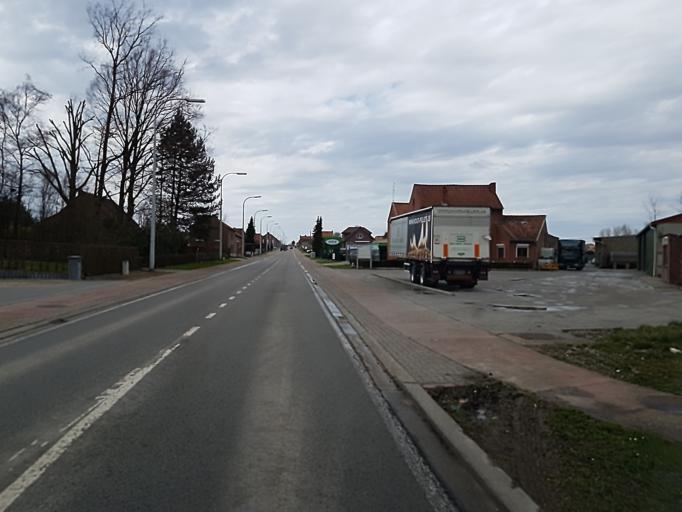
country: BE
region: Flanders
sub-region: Provincie Limburg
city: Borgloon
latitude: 50.7857
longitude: 5.4026
